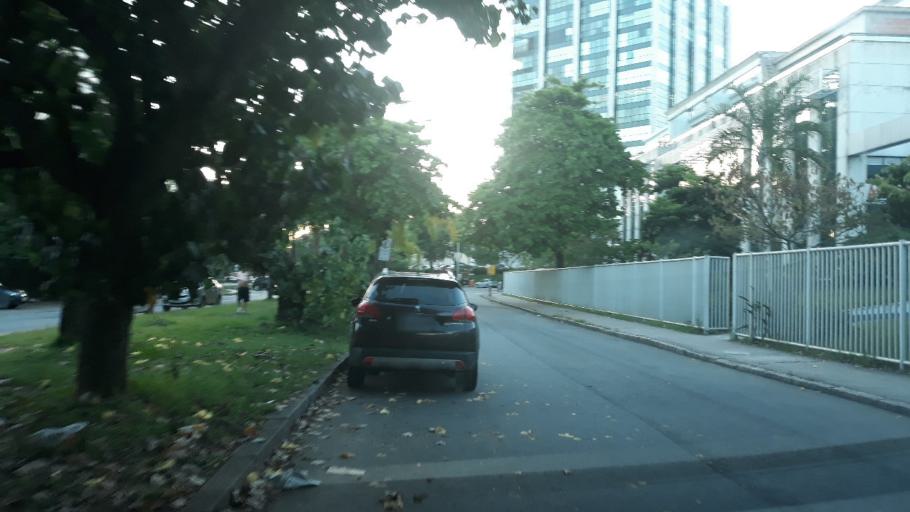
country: BR
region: Rio de Janeiro
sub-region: Rio De Janeiro
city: Rio de Janeiro
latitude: -23.0013
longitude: -43.3464
